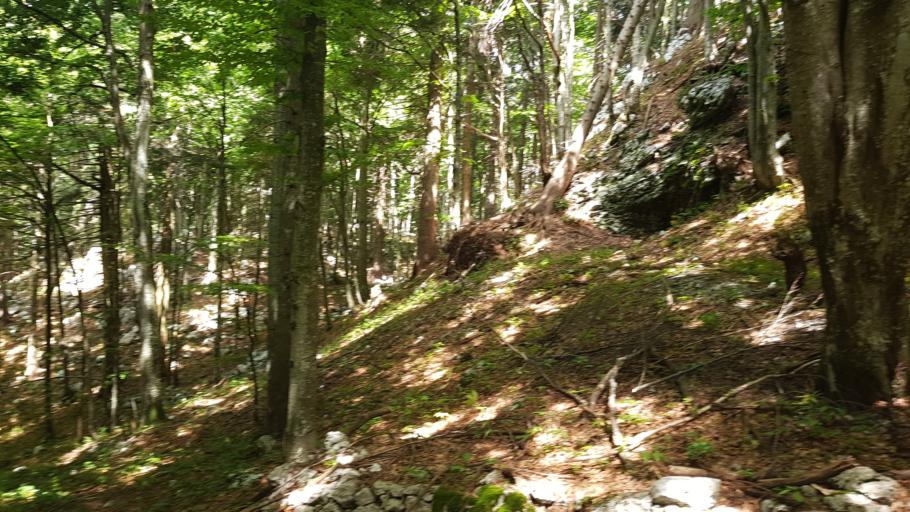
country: SI
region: Bovec
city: Bovec
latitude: 46.3068
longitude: 13.5063
